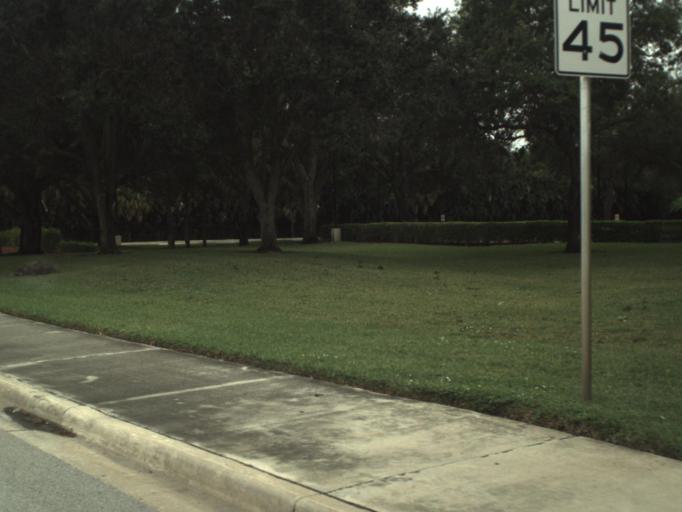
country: US
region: Florida
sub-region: Palm Beach County
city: North Palm Beach
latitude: 26.8226
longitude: -80.1059
